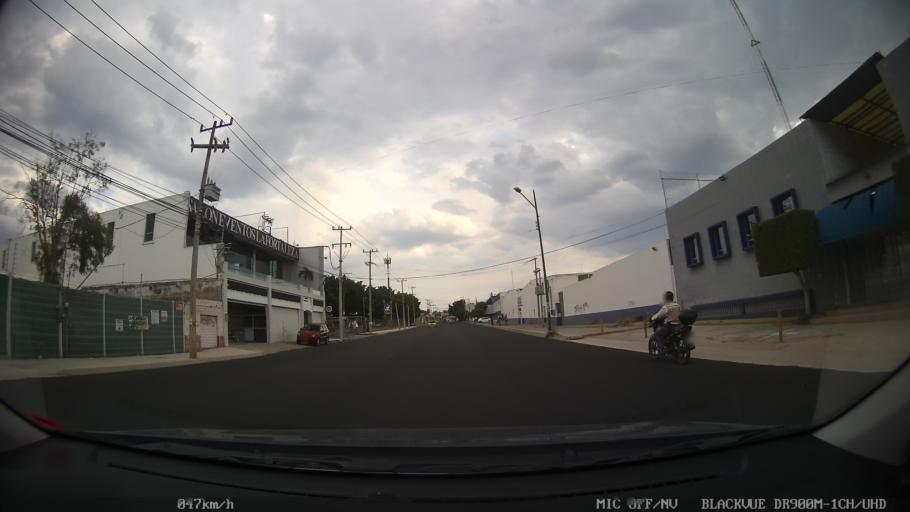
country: MX
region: Jalisco
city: Tlaquepaque
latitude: 20.6203
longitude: -103.2820
